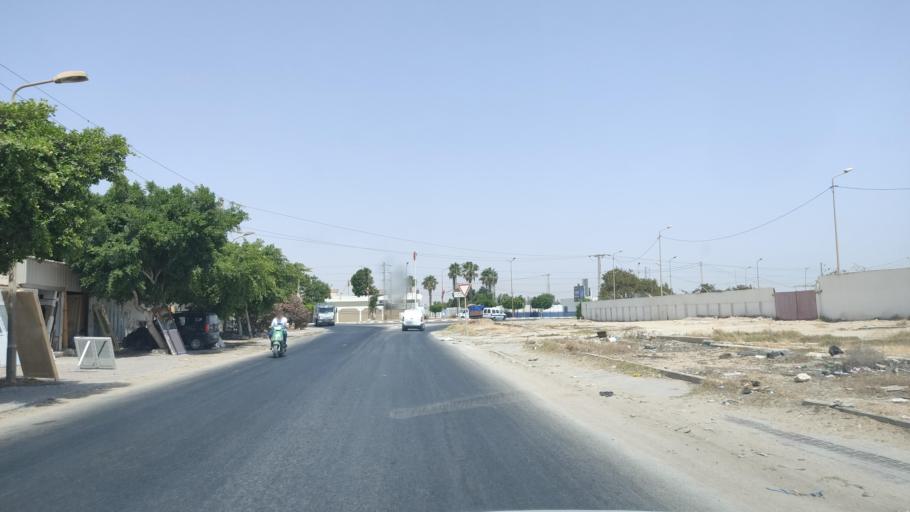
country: TN
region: Safaqis
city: Sfax
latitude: 34.6988
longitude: 10.7193
